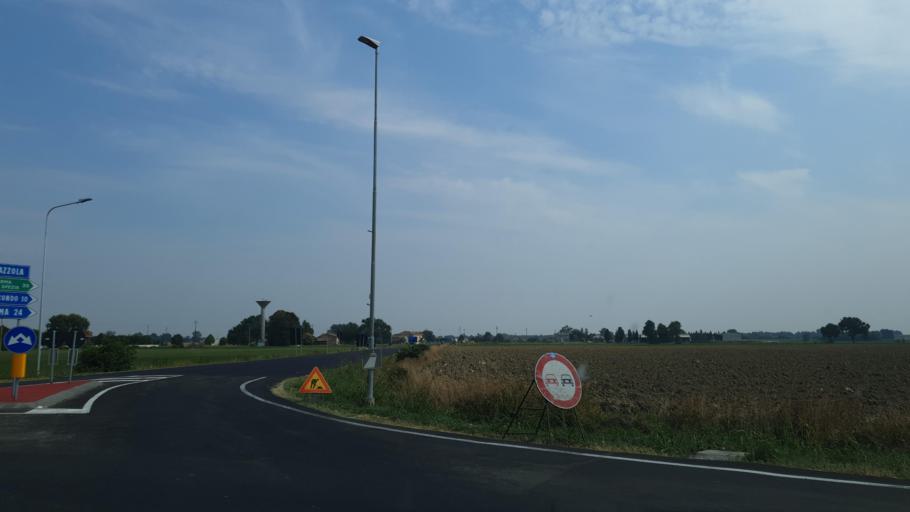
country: IT
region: Emilia-Romagna
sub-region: Provincia di Parma
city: Roccabianca
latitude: 45.0071
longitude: 10.1896
